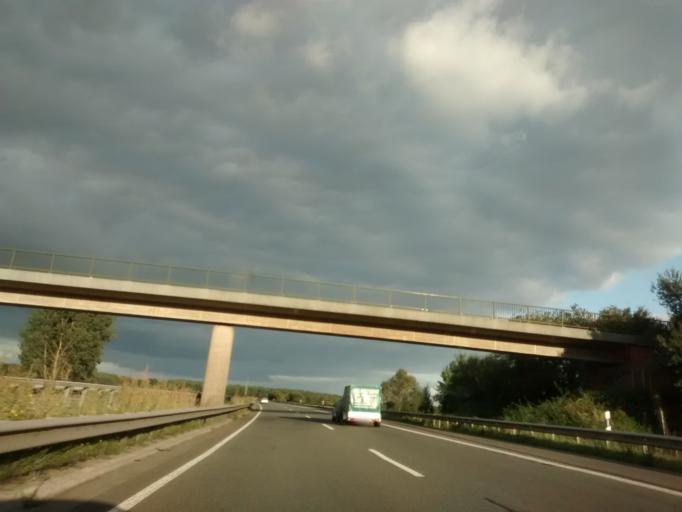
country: DE
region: Lower Saxony
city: Salzbergen
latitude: 52.3366
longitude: 7.3074
